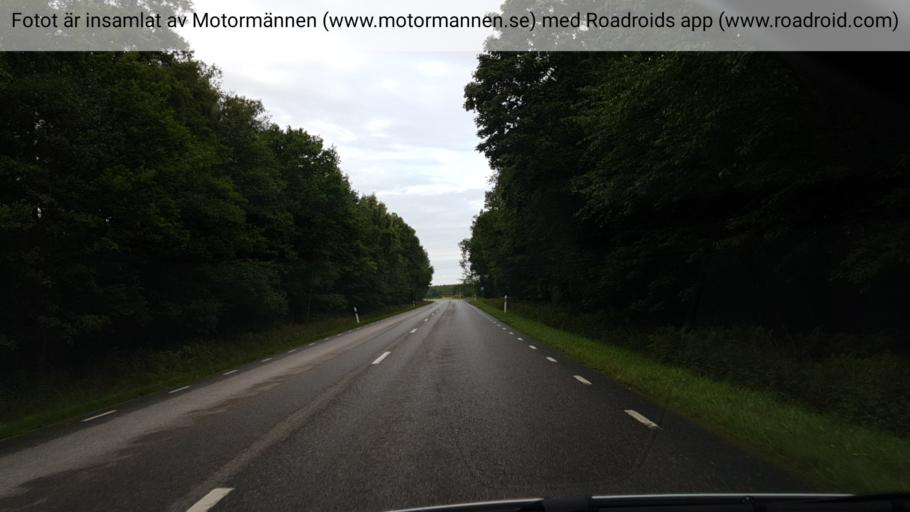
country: SE
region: Vaestra Goetaland
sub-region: Hjo Kommun
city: Hjo
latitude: 58.2355
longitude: 14.2221
